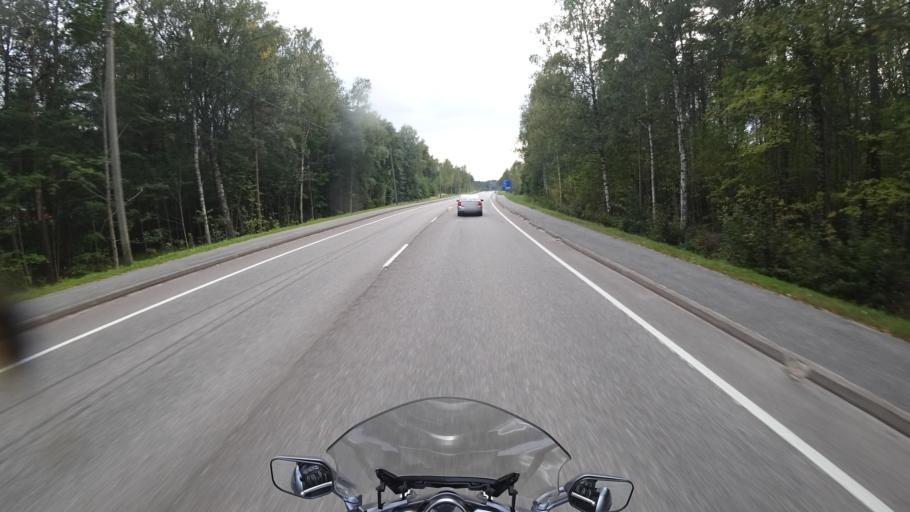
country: FI
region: Uusimaa
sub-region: Raaseporin
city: Karis
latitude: 60.0763
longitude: 23.6582
